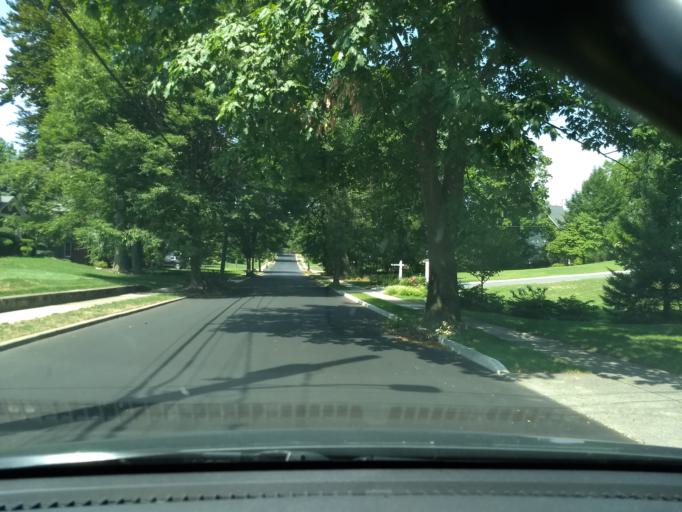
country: US
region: New Jersey
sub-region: Bergen County
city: Ridgewood
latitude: 40.9742
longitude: -74.1121
